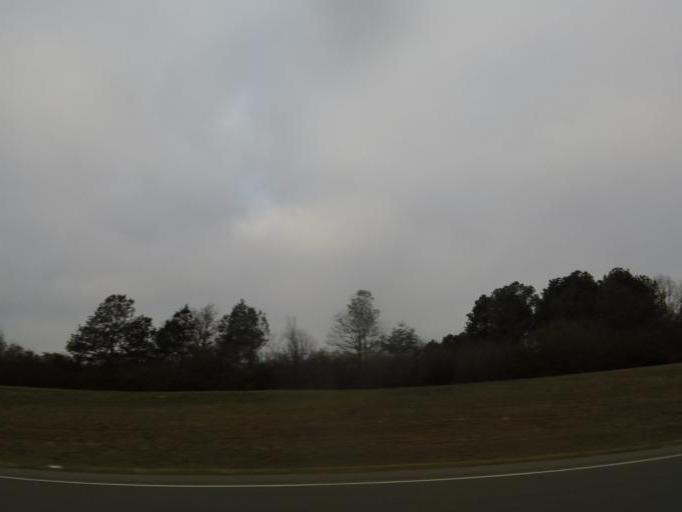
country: US
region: Alabama
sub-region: Jefferson County
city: Gardendale
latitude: 33.6667
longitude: -86.8319
